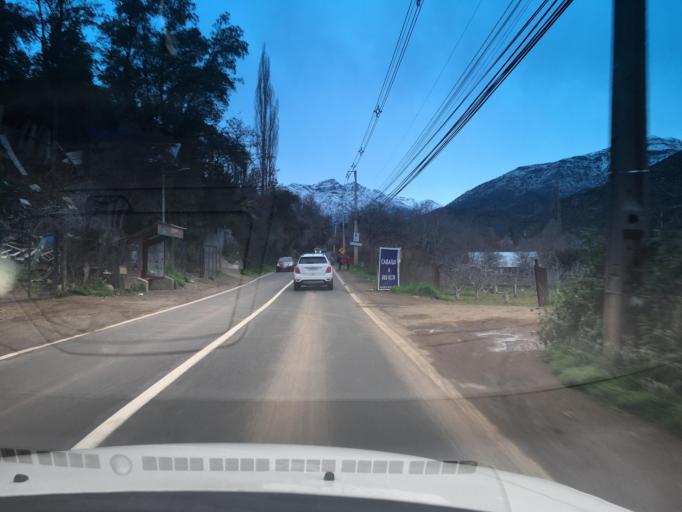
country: CL
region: Santiago Metropolitan
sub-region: Provincia de Cordillera
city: Puente Alto
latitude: -33.6620
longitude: -70.3501
